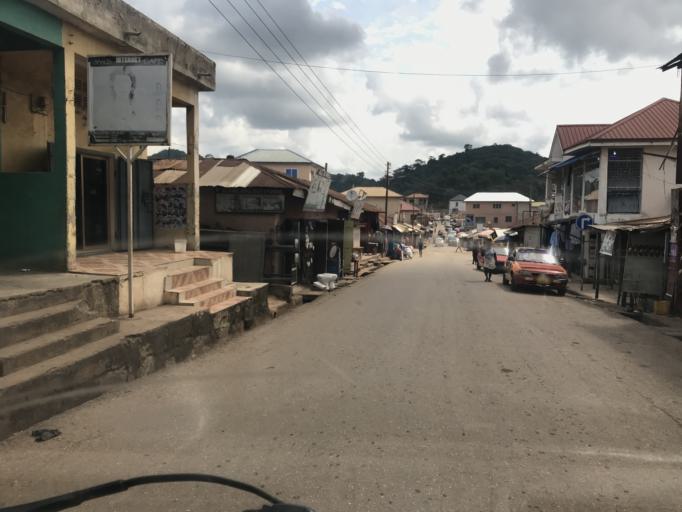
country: GH
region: Ashanti
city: Obuasi
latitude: 6.2008
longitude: -1.6652
